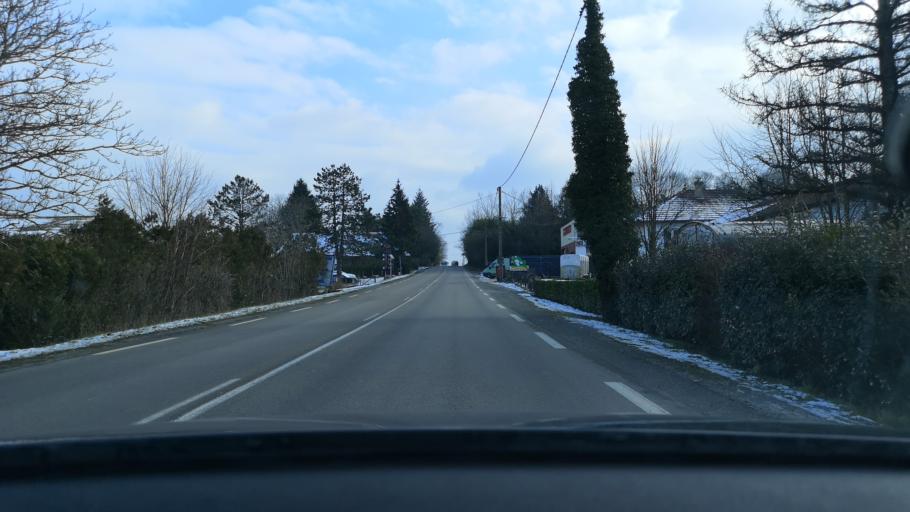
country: FR
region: Franche-Comte
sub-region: Departement du Jura
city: Bletterans
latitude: 46.6712
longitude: 5.3958
